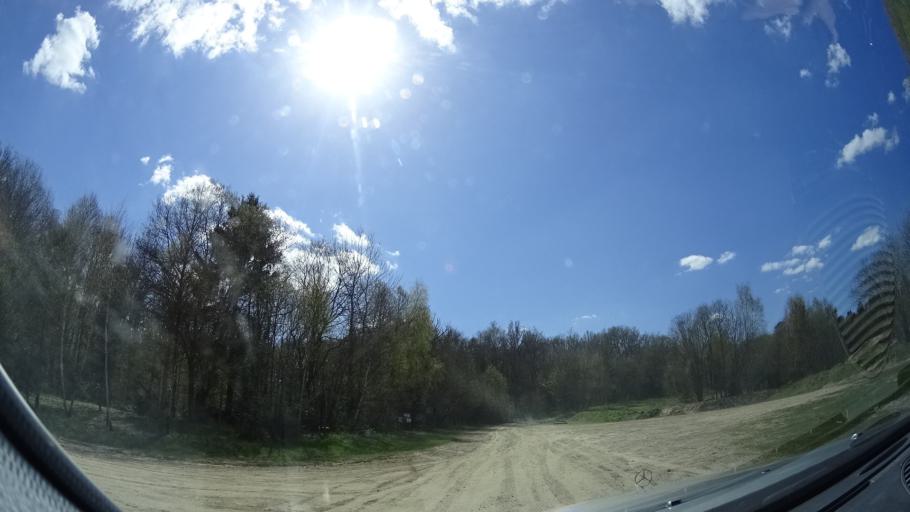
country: SE
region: Skane
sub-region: Hassleholms Kommun
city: Tormestorp
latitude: 56.0916
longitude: 13.7189
